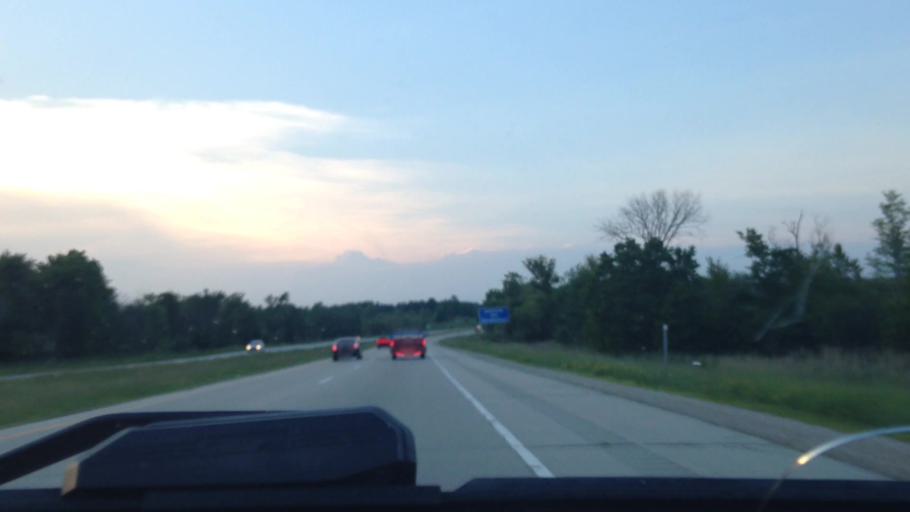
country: US
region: Wisconsin
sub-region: Washington County
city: Jackson
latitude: 43.3659
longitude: -88.1929
